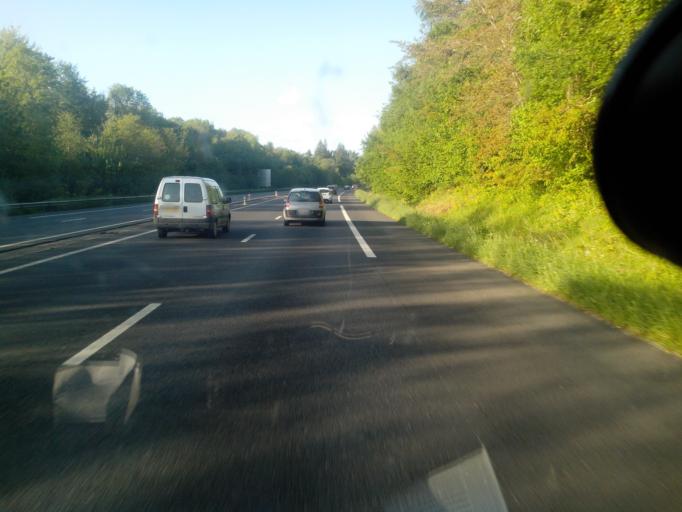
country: FR
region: Haute-Normandie
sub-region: Departement de la Seine-Maritime
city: Saint-Saens
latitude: 49.6688
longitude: 1.3149
